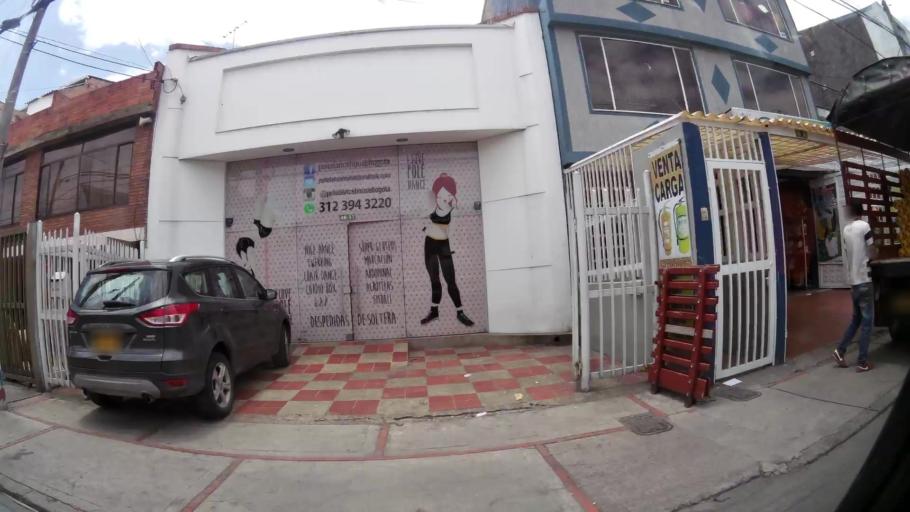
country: CO
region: Bogota D.C.
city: Barrio San Luis
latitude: 4.7183
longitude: -74.0544
